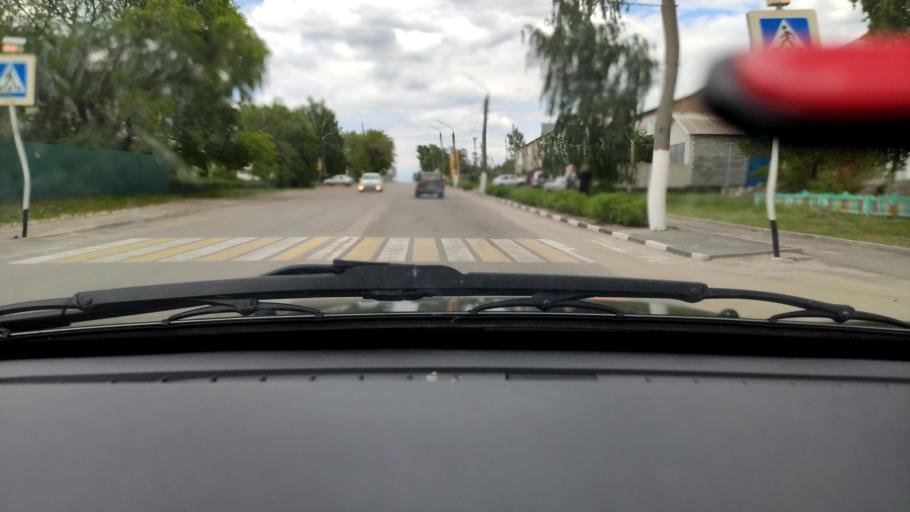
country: RU
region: Voronezj
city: Rossosh'
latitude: 51.0846
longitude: 38.6441
